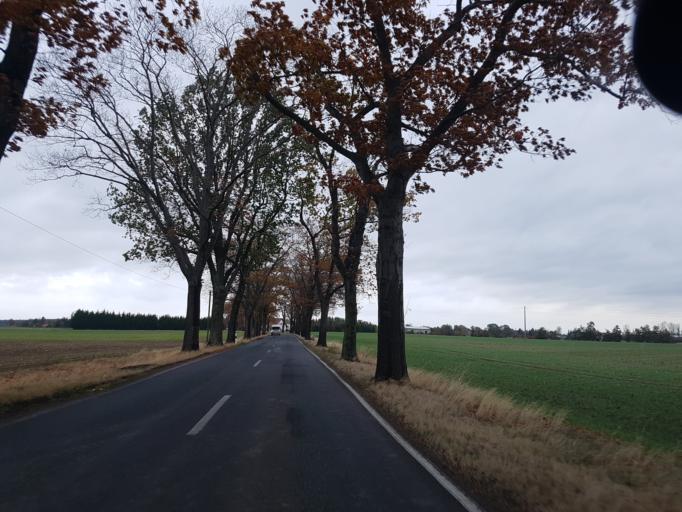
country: DE
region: Brandenburg
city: Falkenberg
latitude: 51.6286
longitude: 13.2321
